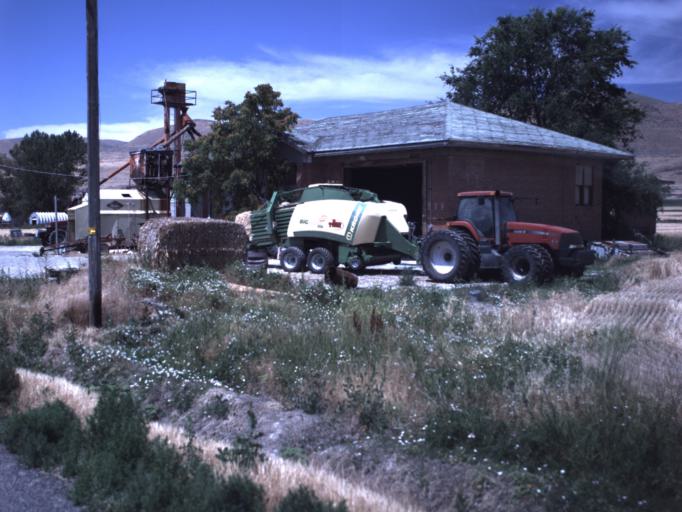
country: US
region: Utah
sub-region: Box Elder County
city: Tremonton
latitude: 41.6508
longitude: -112.3011
